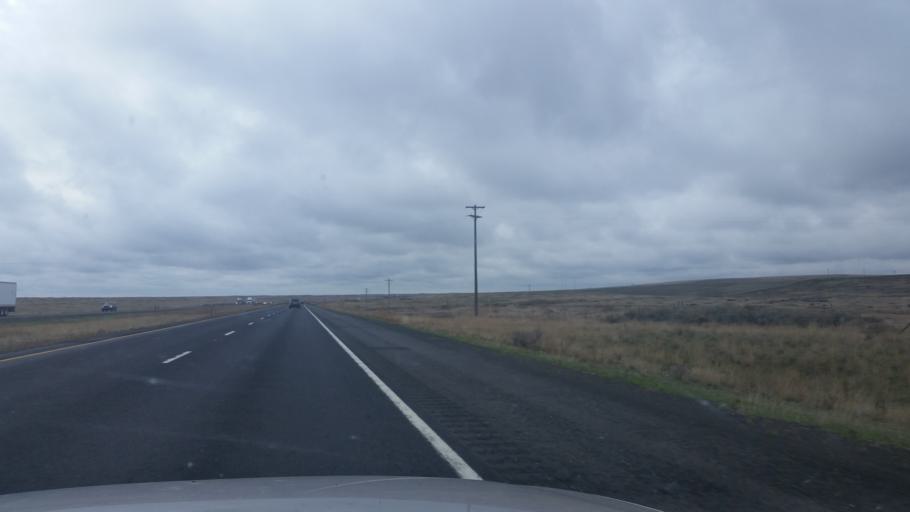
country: US
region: Washington
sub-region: Spokane County
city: Medical Lake
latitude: 47.3437
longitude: -117.9055
